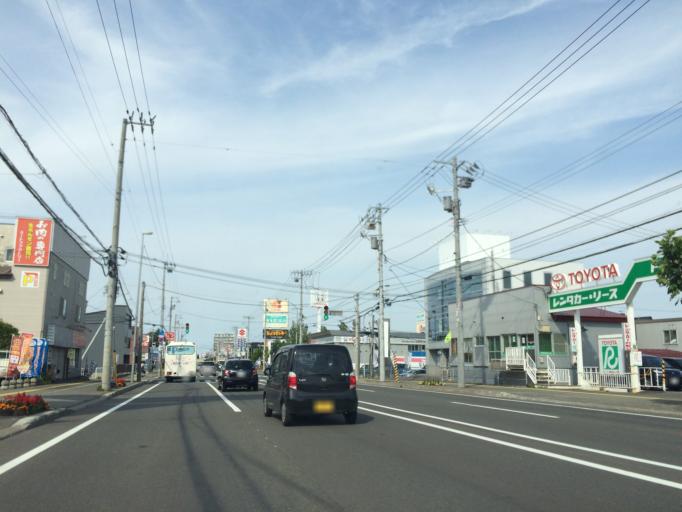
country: JP
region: Hokkaido
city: Ebetsu
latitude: 43.0894
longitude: 141.5183
